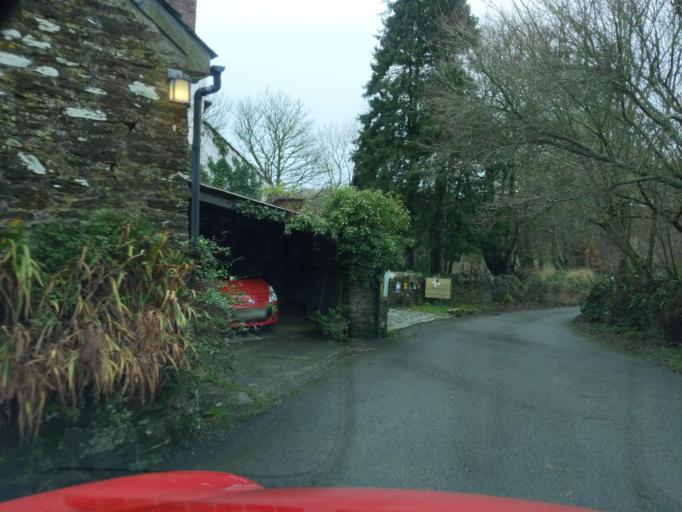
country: GB
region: England
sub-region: Cornwall
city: Duloe
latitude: 50.3521
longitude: -4.5123
